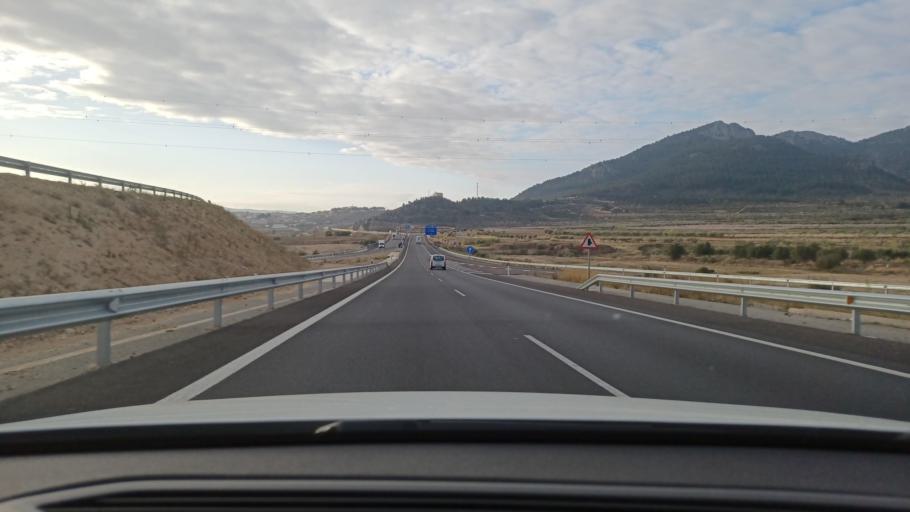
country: ES
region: Valencia
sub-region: Provincia de Valencia
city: La Font de la Figuera
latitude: 38.8258
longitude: -0.8921
